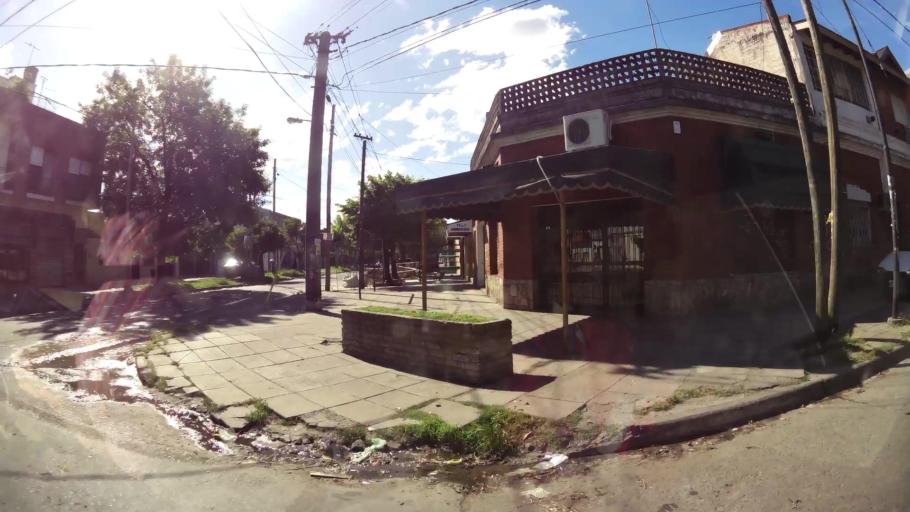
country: AR
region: Buenos Aires
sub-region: Partido de General San Martin
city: General San Martin
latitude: -34.5275
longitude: -58.5757
